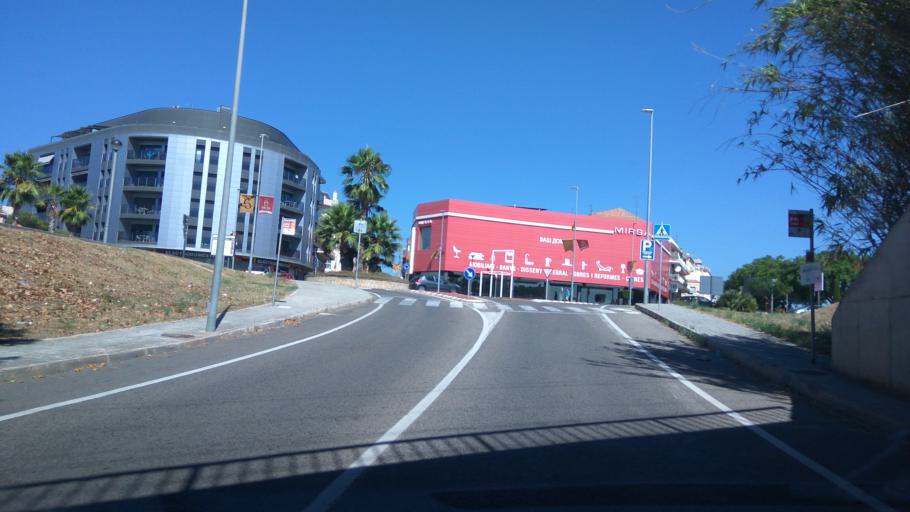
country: ES
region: Catalonia
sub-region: Provincia de Tarragona
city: El Vendrell
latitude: 41.2140
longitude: 1.5354
